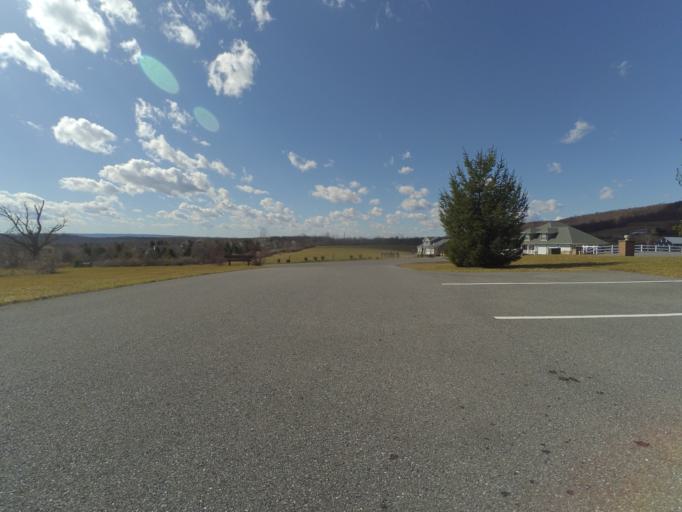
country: US
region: Pennsylvania
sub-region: Centre County
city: Park Forest Village
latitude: 40.8236
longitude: -77.9648
